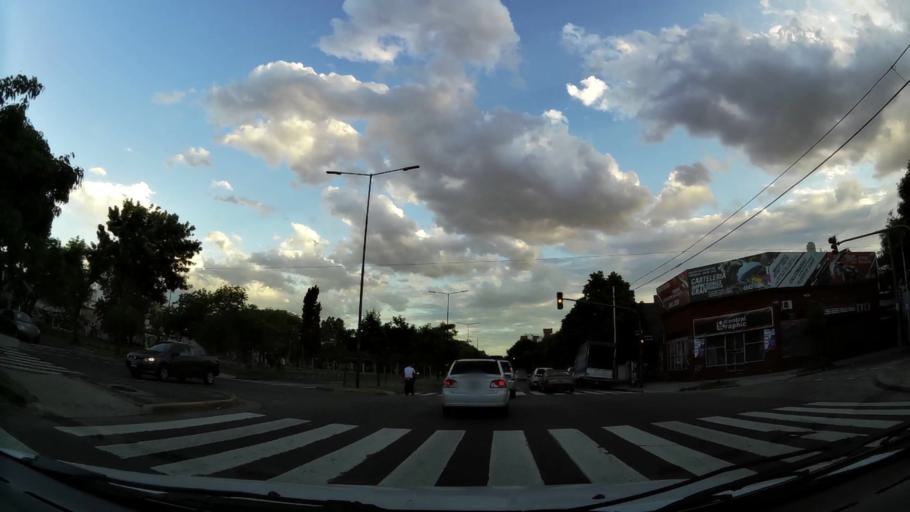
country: AR
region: Buenos Aires
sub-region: Partido de General San Martin
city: General San Martin
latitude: -34.5566
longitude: -58.4876
